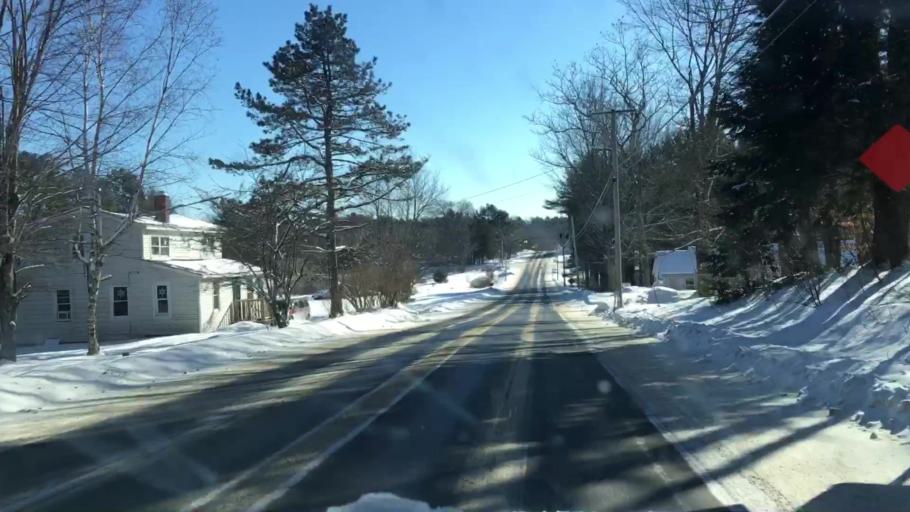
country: US
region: Maine
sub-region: Androscoggin County
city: Lisbon Falls
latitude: 43.9369
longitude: -70.0633
